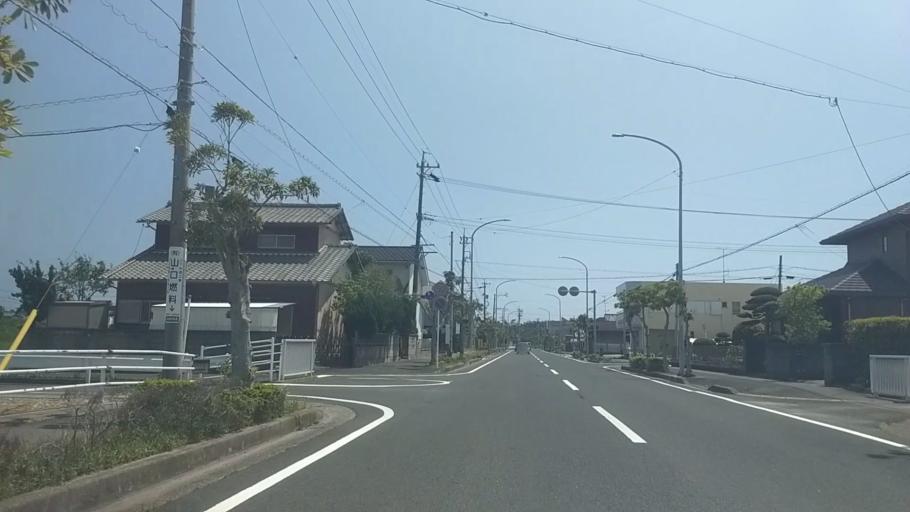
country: JP
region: Shizuoka
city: Kosai-shi
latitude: 34.6849
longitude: 137.5697
